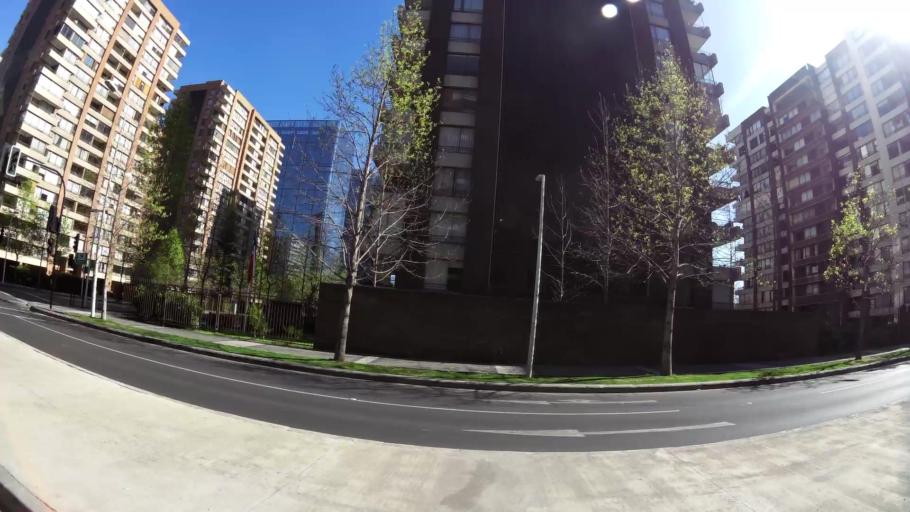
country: CL
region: Santiago Metropolitan
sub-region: Provincia de Santiago
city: Villa Presidente Frei, Nunoa, Santiago, Chile
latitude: -33.4061
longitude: -70.5717
